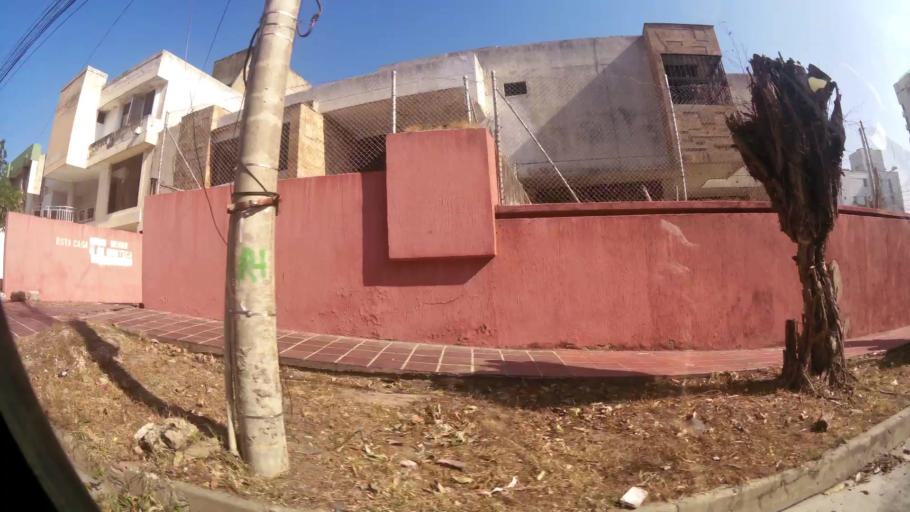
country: CO
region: Atlantico
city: Barranquilla
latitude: 10.9994
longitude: -74.8269
